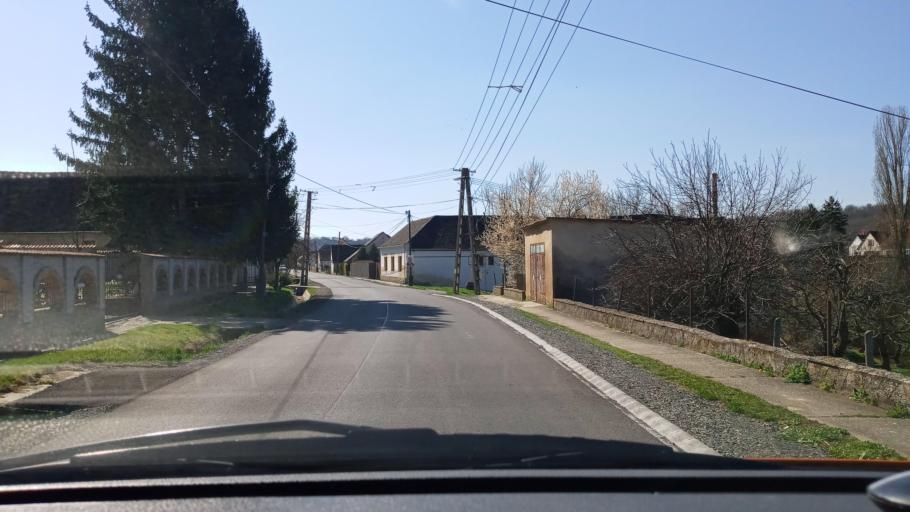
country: HU
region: Baranya
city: Kozarmisleny
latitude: 46.0360
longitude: 18.3878
